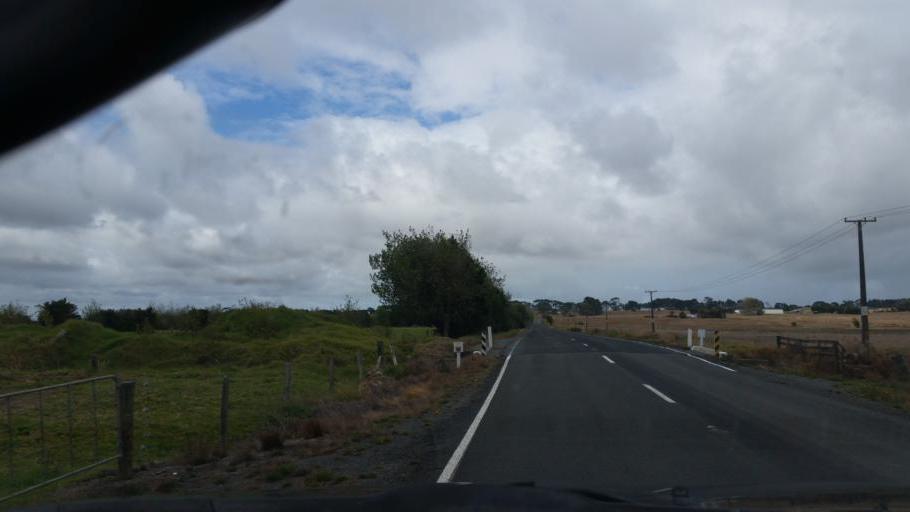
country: NZ
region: Northland
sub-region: Kaipara District
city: Dargaville
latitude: -36.0857
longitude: 173.9530
